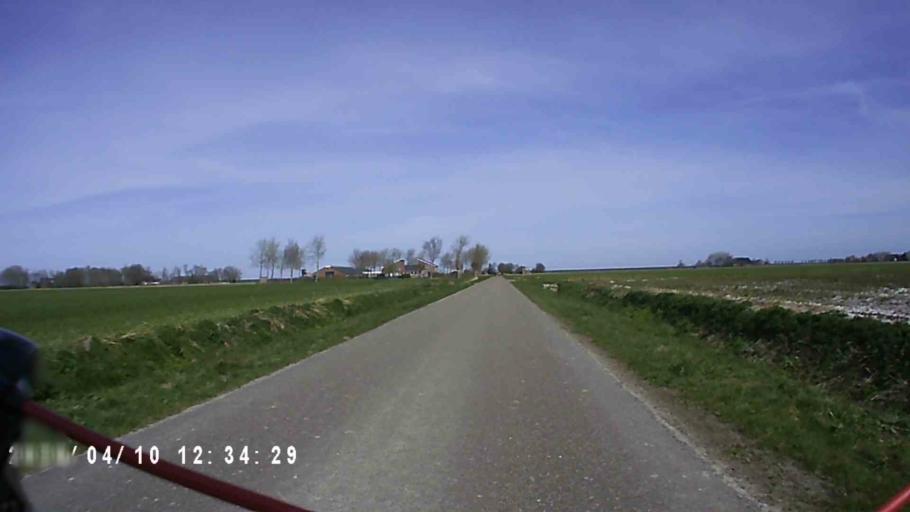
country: NL
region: Groningen
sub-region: Gemeente De Marne
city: Ulrum
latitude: 53.3969
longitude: 6.4167
